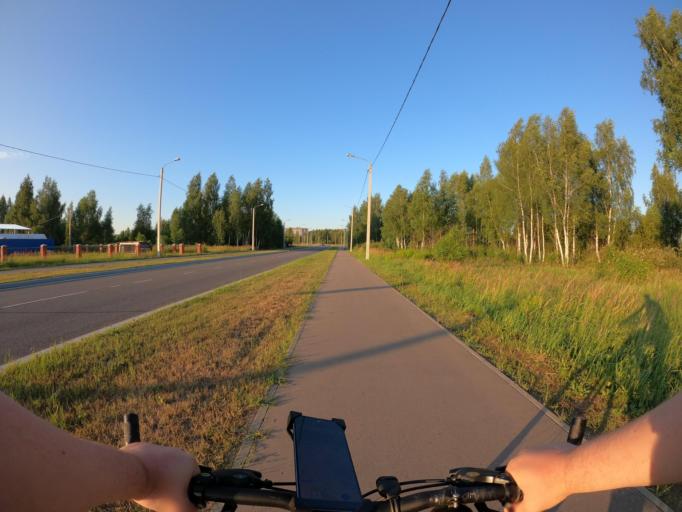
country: RU
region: Moskovskaya
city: Beloozerskiy
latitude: 55.4581
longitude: 38.4268
